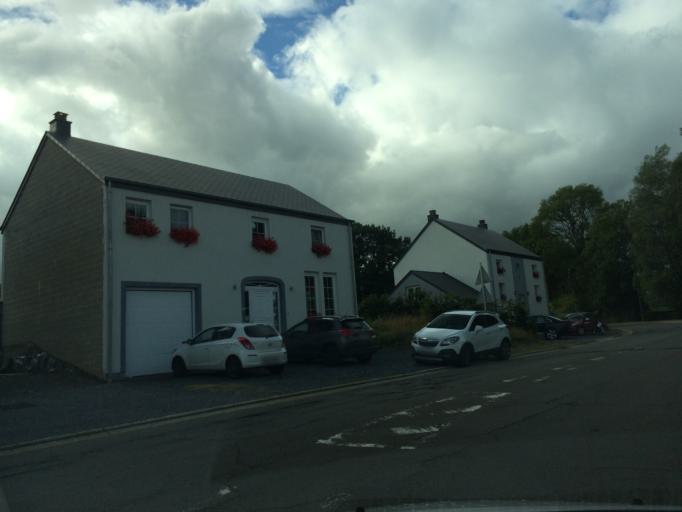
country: BE
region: Wallonia
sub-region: Province du Luxembourg
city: Chiny
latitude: 49.6970
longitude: 5.3749
